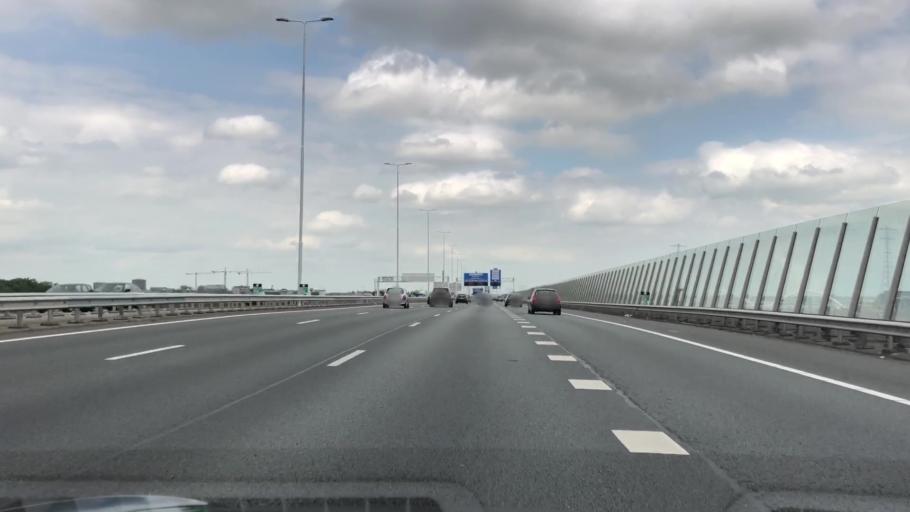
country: NL
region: North Holland
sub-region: Gemeente Diemen
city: Diemen
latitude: 52.3583
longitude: 4.9703
